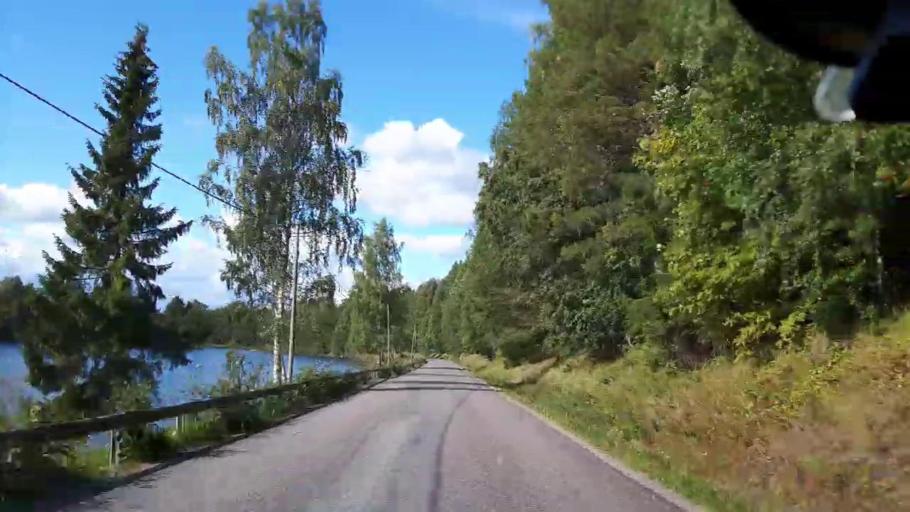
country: SE
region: Jaemtland
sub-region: Braecke Kommun
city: Braecke
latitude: 63.1756
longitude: 15.5620
